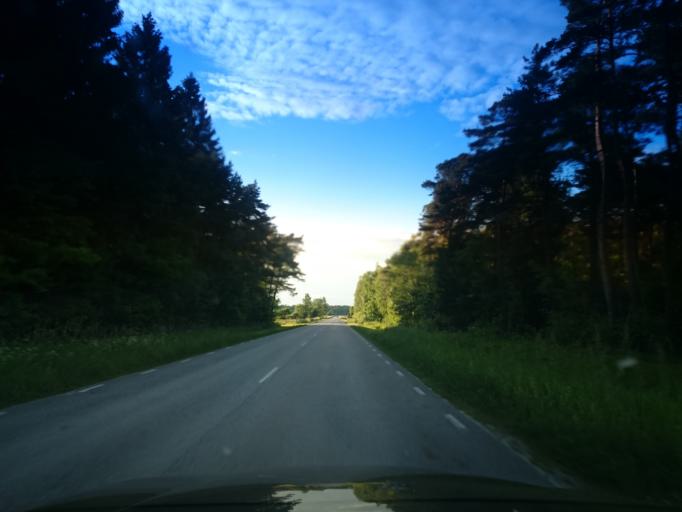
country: SE
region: Gotland
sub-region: Gotland
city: Hemse
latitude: 57.3008
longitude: 18.3830
